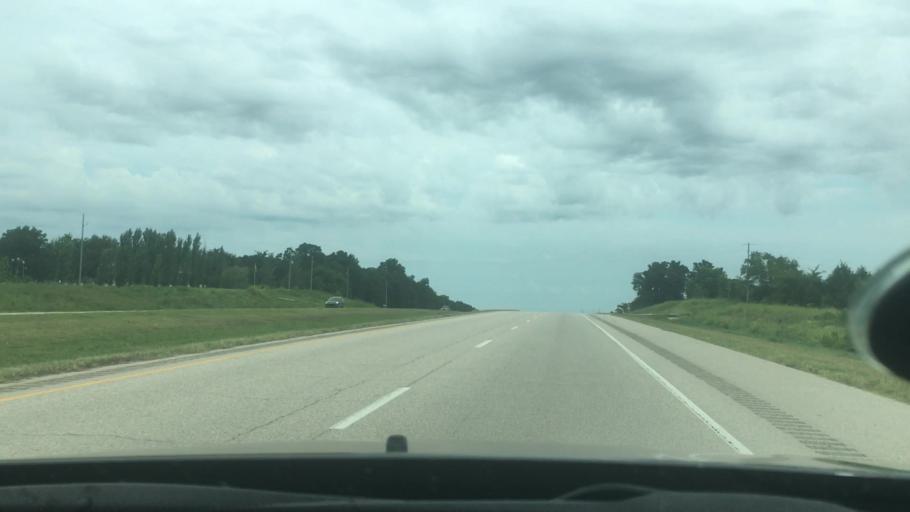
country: US
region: Oklahoma
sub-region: Pontotoc County
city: Byng
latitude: 34.9152
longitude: -96.6804
